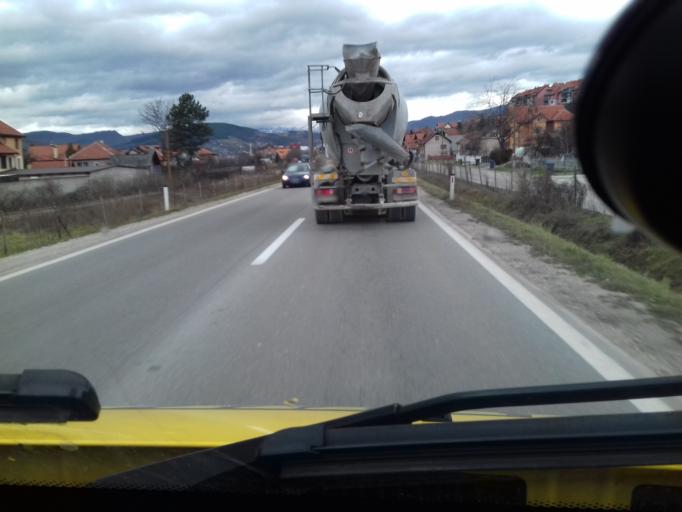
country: BA
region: Federation of Bosnia and Herzegovina
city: Zenica
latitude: 44.1909
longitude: 17.9468
